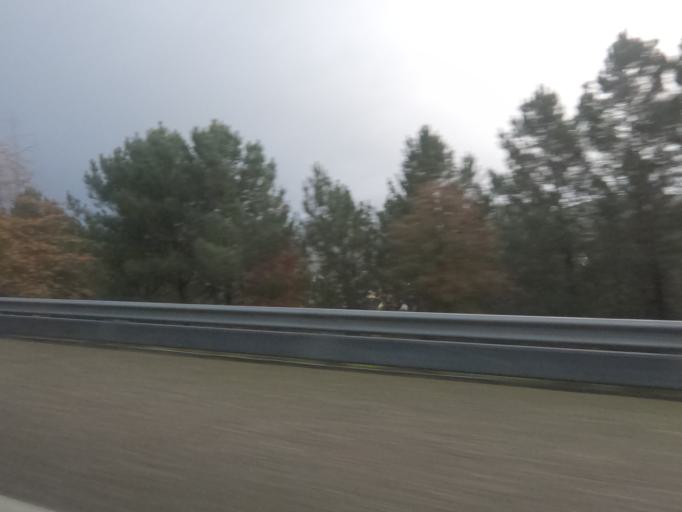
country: PT
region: Viana do Castelo
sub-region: Ponte de Lima
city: Ponte de Lima
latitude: 41.8202
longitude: -8.6002
